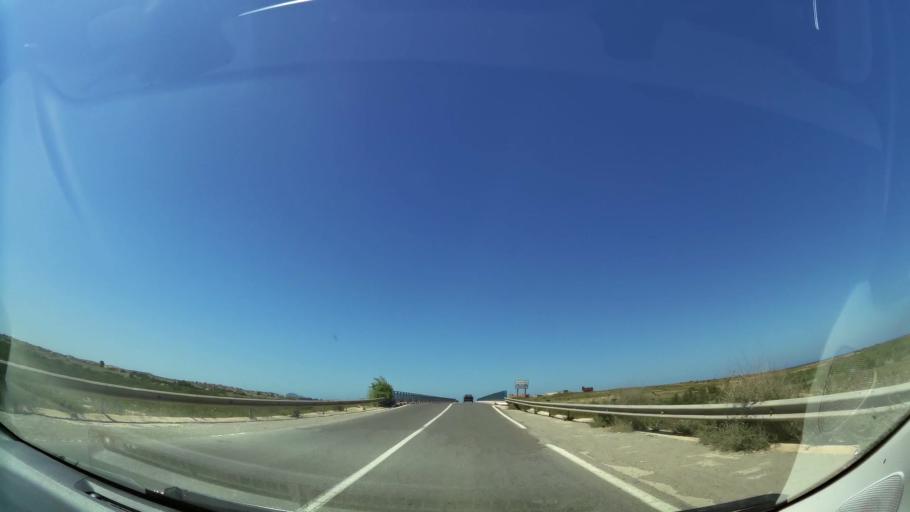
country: MA
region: Oriental
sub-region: Berkane-Taourirt
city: Madagh
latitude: 35.1069
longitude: -2.3613
